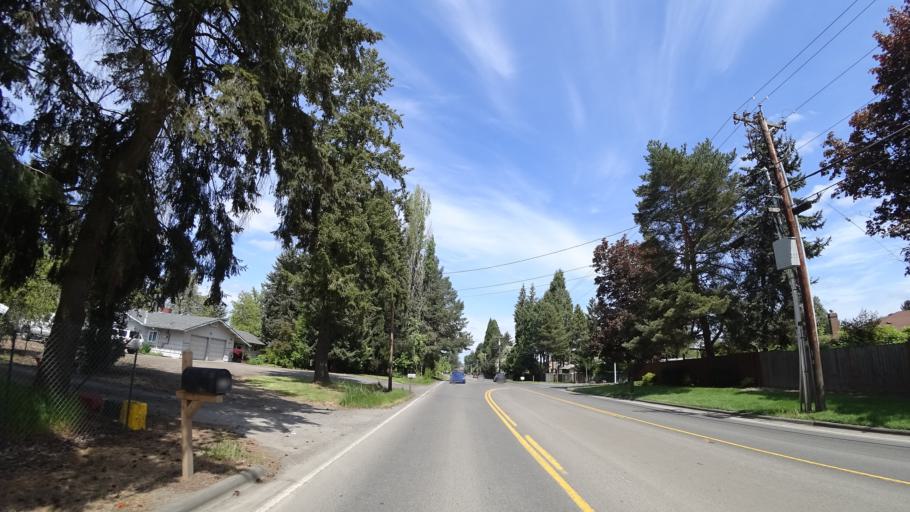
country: US
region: Oregon
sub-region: Washington County
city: Aloha
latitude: 45.4774
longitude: -122.8945
